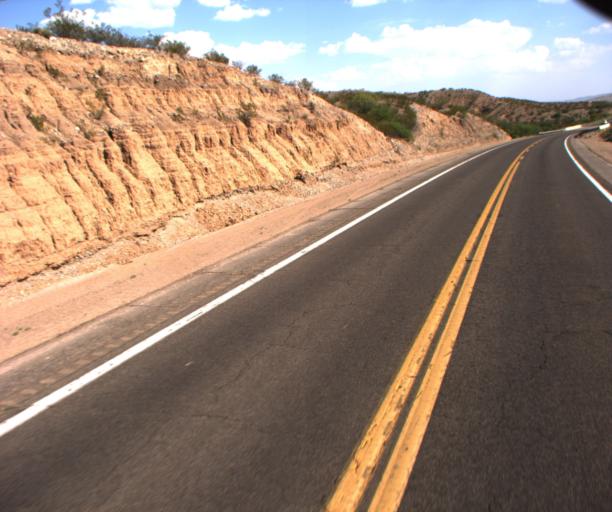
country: US
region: Arizona
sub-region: Greenlee County
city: Clifton
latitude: 32.8096
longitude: -109.1679
